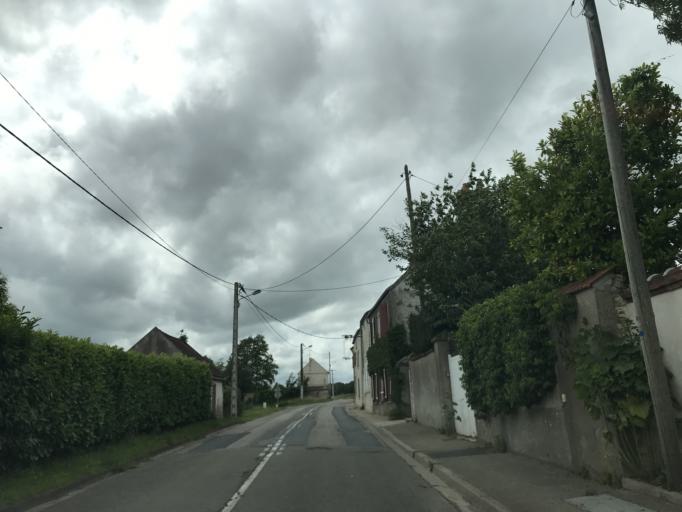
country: FR
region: Ile-de-France
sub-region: Departement des Yvelines
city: Rosny-sur-Seine
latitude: 48.9755
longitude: 1.5858
